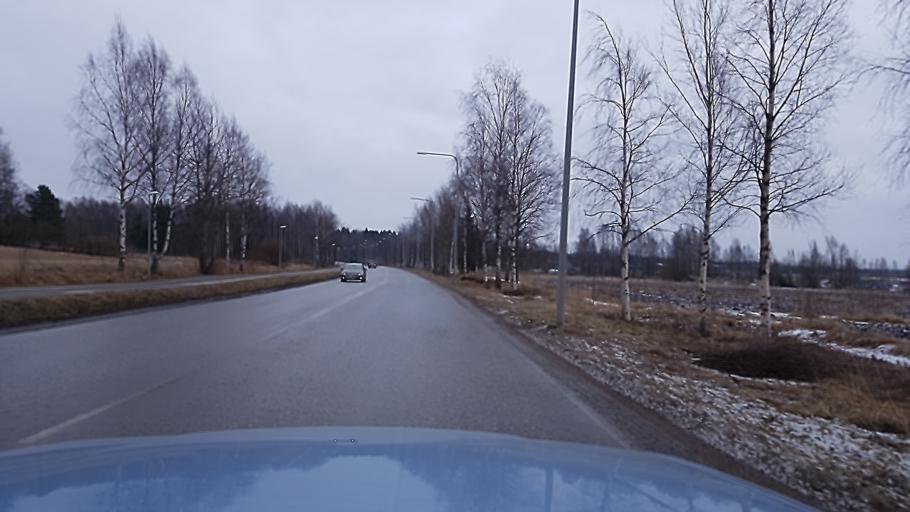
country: FI
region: Uusimaa
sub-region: Helsinki
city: Vantaa
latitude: 60.2647
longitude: 25.0472
